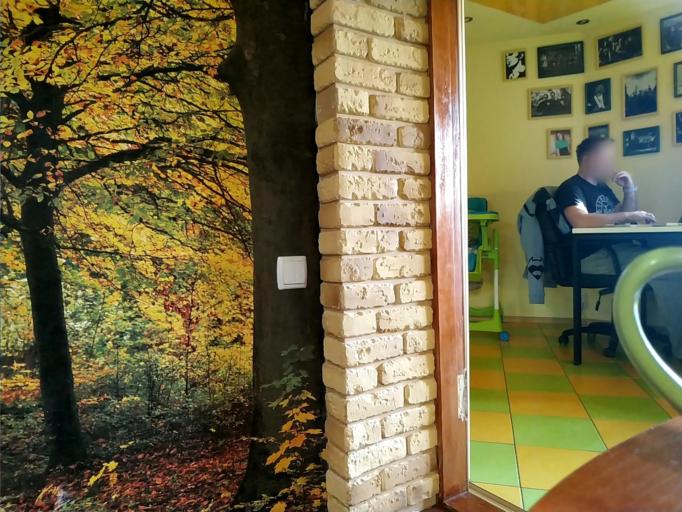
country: RU
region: Jaroslavl
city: Krasnyy Profintern
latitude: 57.8680
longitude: 40.6057
